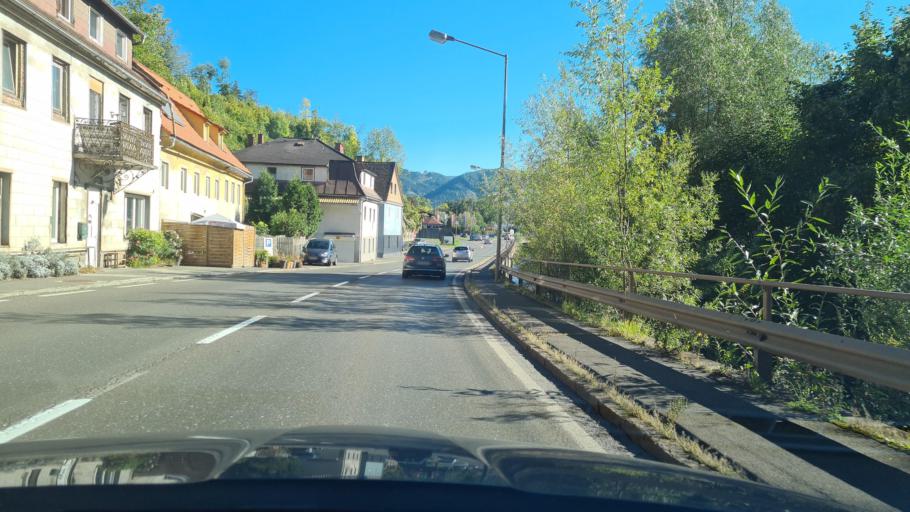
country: AT
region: Styria
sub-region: Politischer Bezirk Leoben
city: Leoben
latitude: 47.3783
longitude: 15.0793
